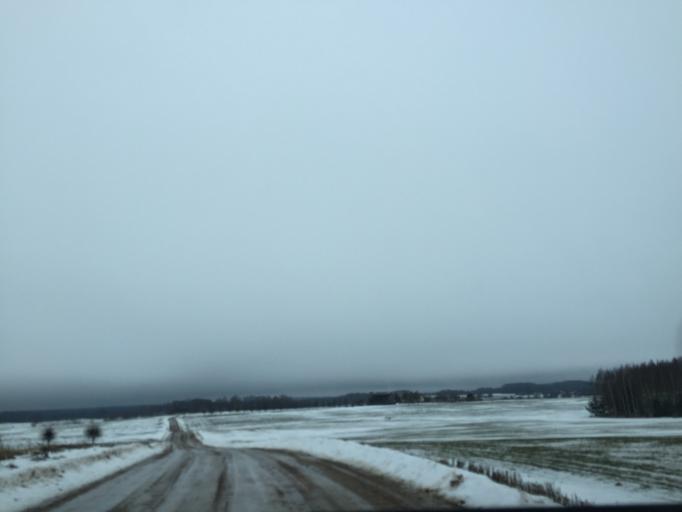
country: LV
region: Krimulda
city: Ragana
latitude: 57.1643
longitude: 24.7224
